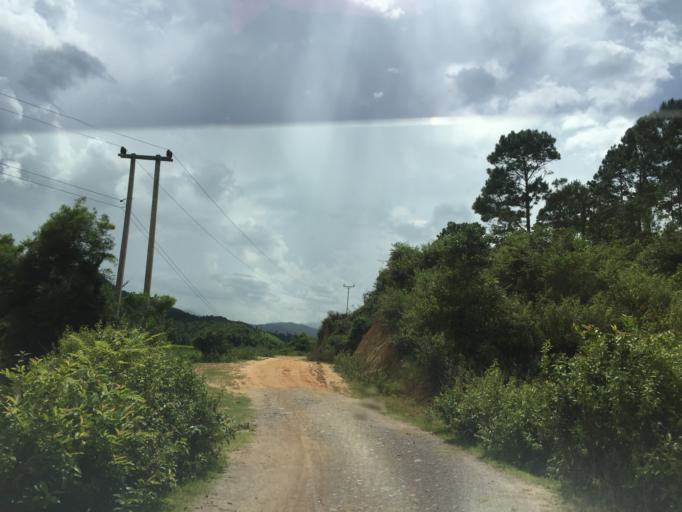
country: LA
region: Xiangkhoang
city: Muang Phonsavan
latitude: 19.3419
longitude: 103.5580
